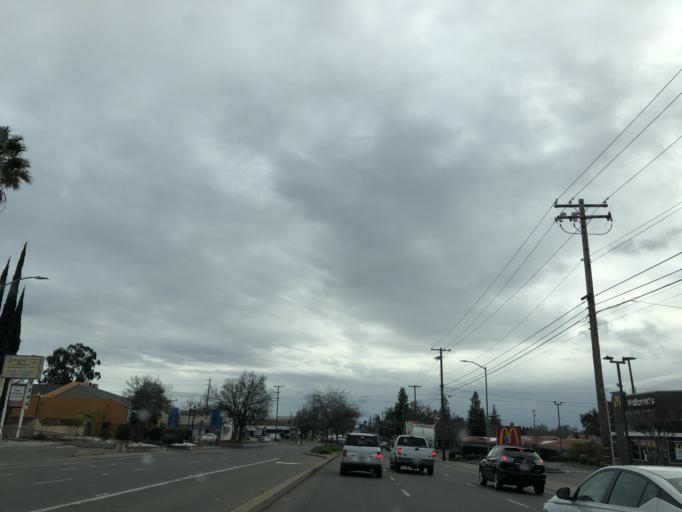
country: US
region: California
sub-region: Sacramento County
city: Carmichael
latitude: 38.6350
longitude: -121.3282
